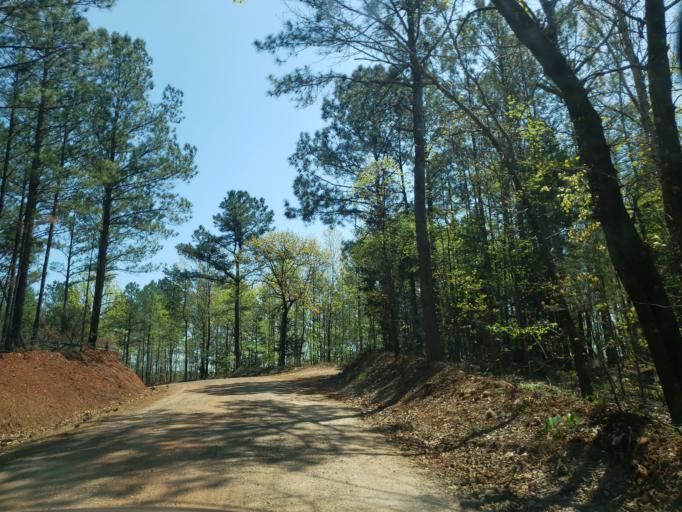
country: US
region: Alabama
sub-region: Tallapoosa County
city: Camp Hill
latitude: 32.6494
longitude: -85.6534
